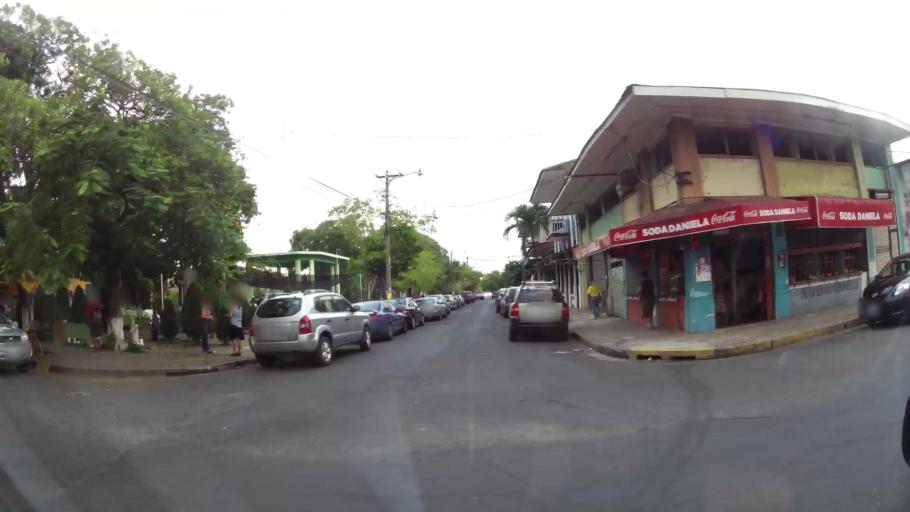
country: CR
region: Puntarenas
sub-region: Canton Central de Puntarenas
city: Puntarenas
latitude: 9.9786
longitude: -84.8336
